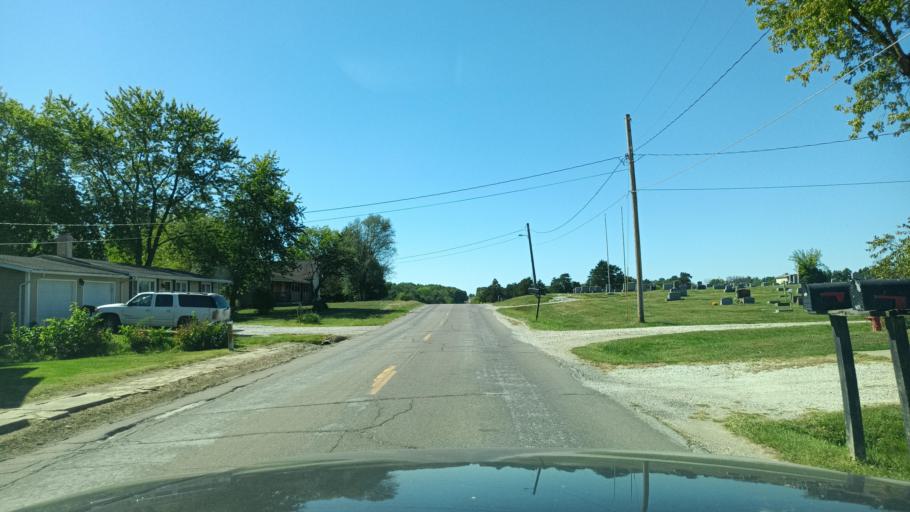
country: US
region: Missouri
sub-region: Macon County
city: La Plata
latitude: 40.0211
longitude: -92.4964
